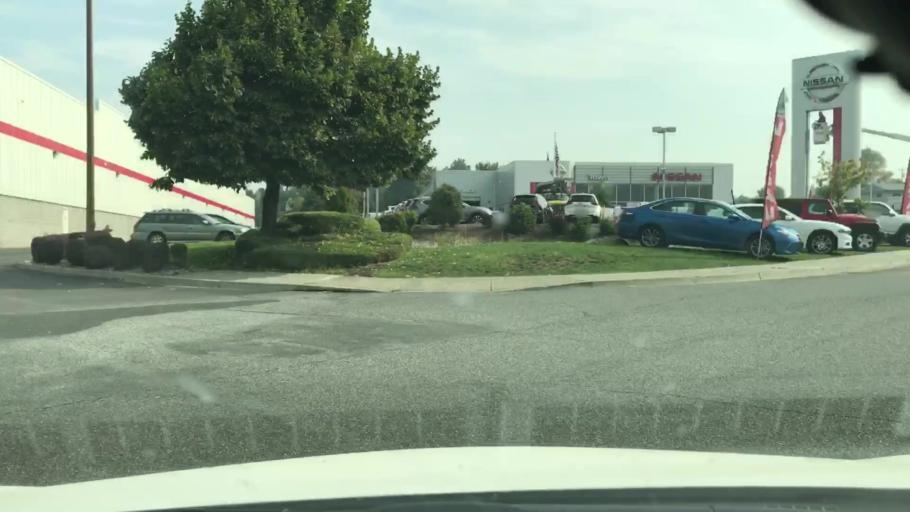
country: US
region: Washington
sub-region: Chelan County
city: South Wenatchee
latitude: 47.4003
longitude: -120.2802
